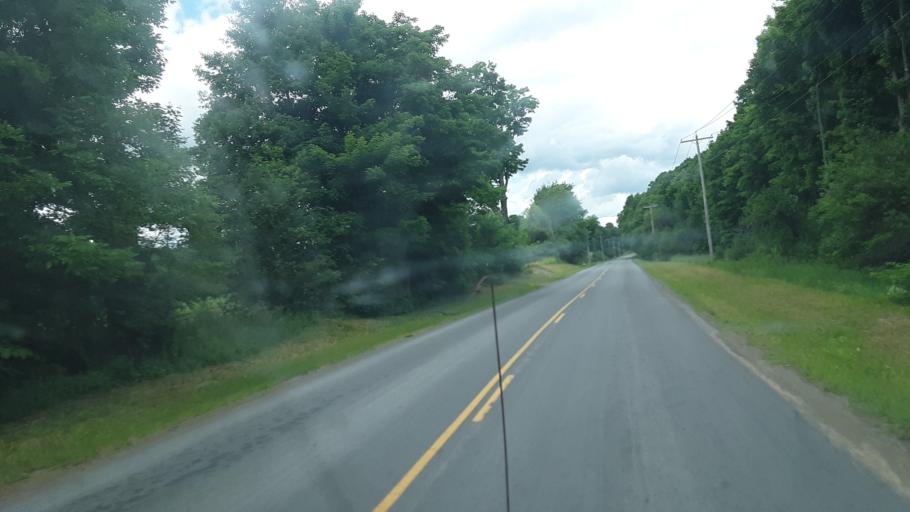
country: US
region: New York
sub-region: Oneida County
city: Rome
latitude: 43.3881
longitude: -75.5522
